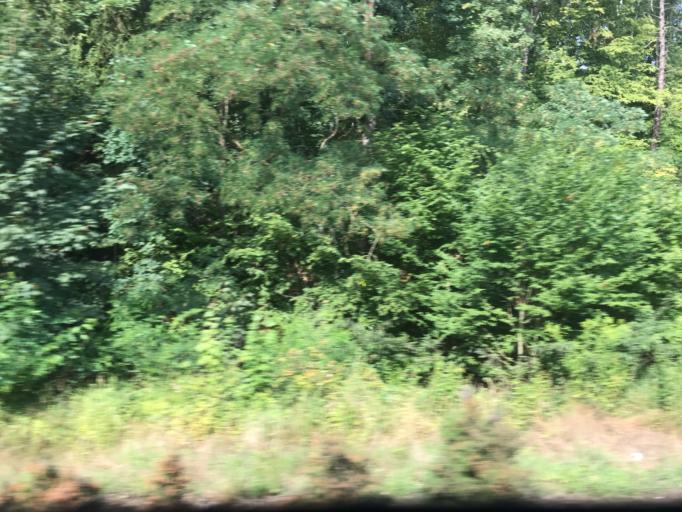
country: CZ
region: Central Bohemia
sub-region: Okres Benesov
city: Cercany
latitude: 49.8821
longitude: 14.7268
